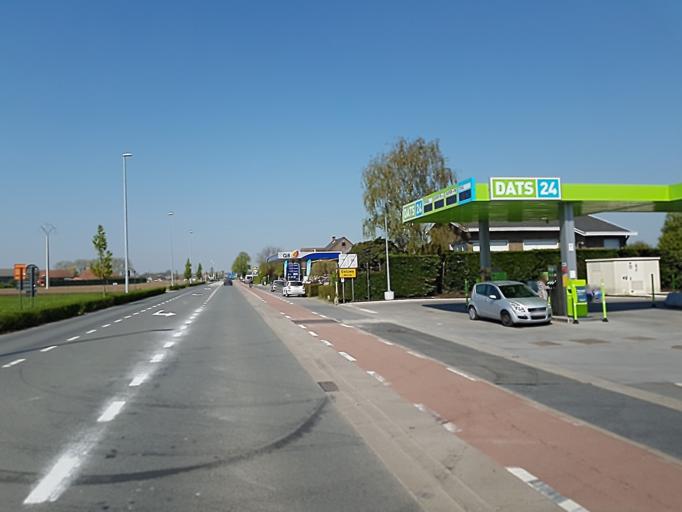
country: BE
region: Flanders
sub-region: Provincie West-Vlaanderen
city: Menen
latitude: 50.8043
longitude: 3.0962
